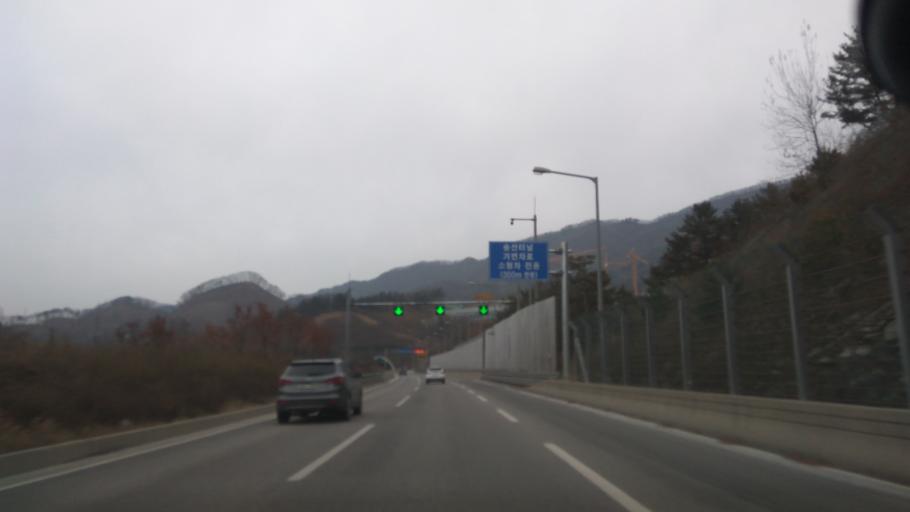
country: KR
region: Gyeonggi-do
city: Cheongpyeong
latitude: 37.6828
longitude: 127.5308
